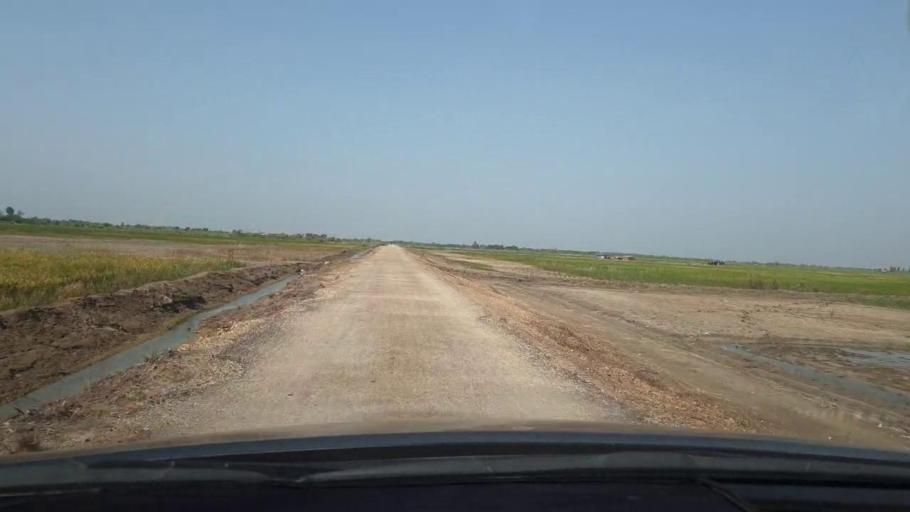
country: PK
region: Sindh
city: Tando Bago
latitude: 24.7179
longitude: 69.1147
